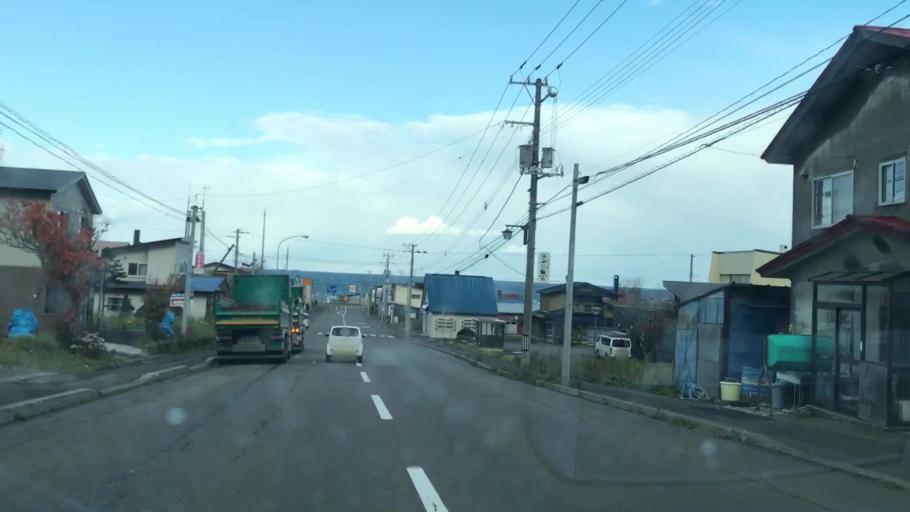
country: JP
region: Hokkaido
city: Yoichi
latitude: 43.3403
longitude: 140.4585
